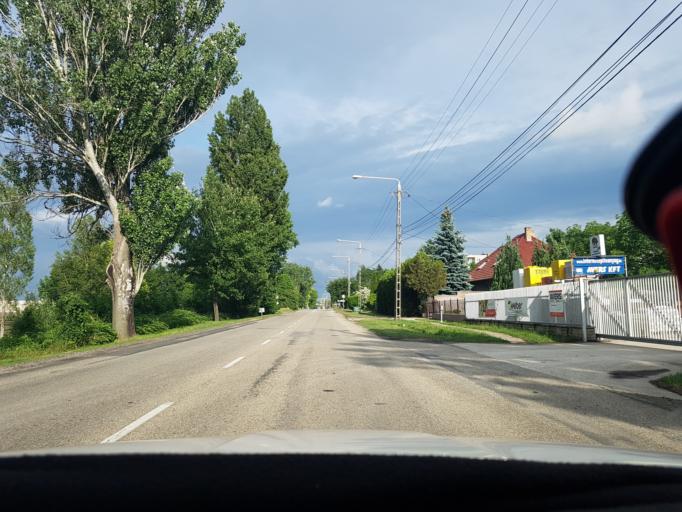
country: HU
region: Komarom-Esztergom
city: Sutto
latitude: 47.7550
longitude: 18.4643
